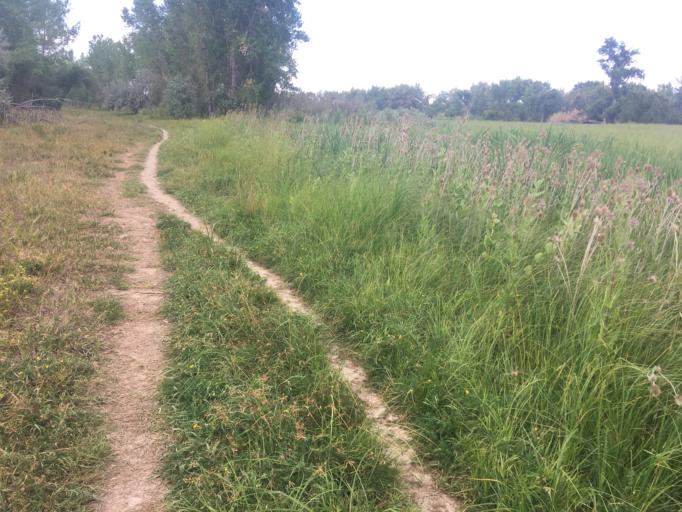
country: US
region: Colorado
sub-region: Boulder County
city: Superior
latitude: 39.9725
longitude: -105.2260
